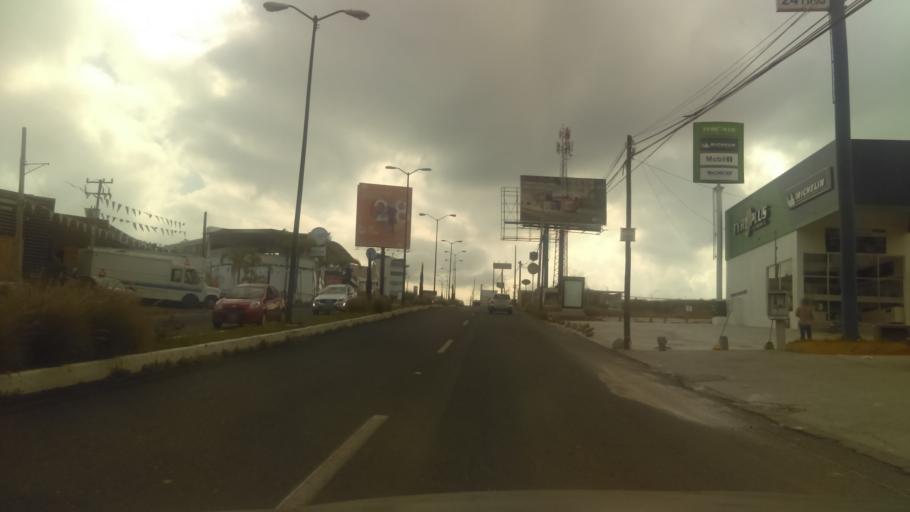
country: MX
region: Michoacan
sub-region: Morelia
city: Montana Monarca (Punta Altozano)
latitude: 19.6703
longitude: -101.1711
